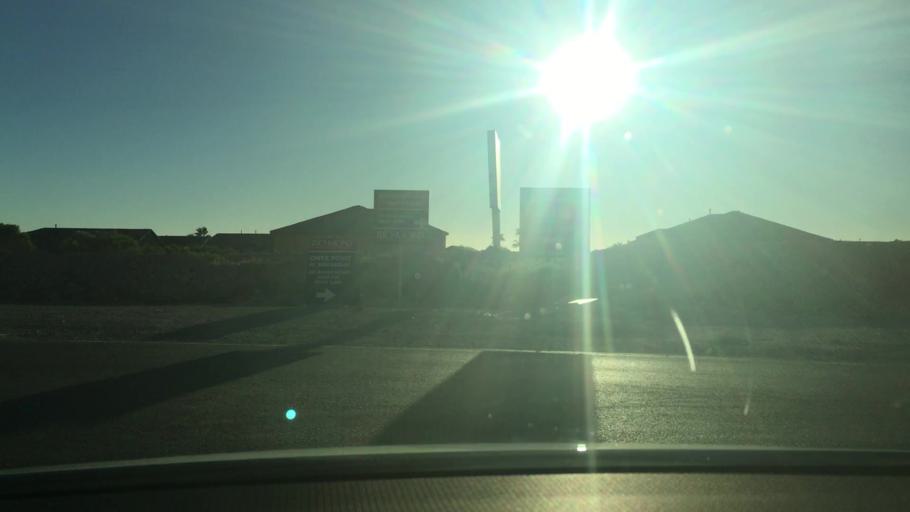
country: US
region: Nevada
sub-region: Clark County
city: Summerlin South
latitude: 36.0736
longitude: -115.3158
